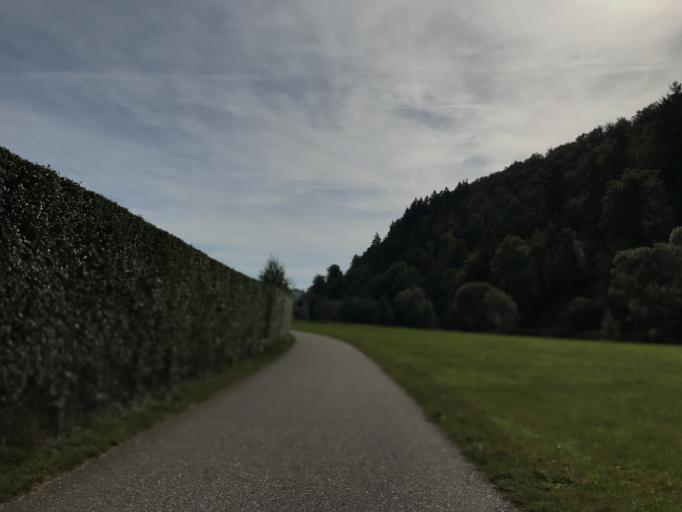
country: DE
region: Baden-Wuerttemberg
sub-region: Freiburg Region
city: Schopfheim
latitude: 47.6604
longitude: 7.8300
